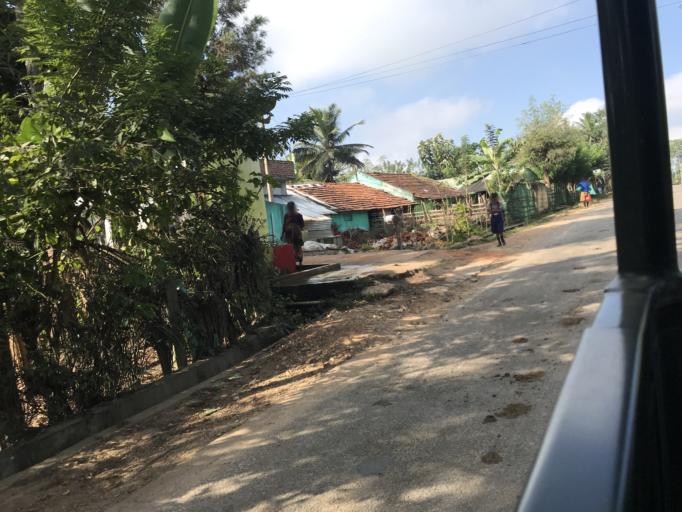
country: IN
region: Karnataka
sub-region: Mysore
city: Heggadadevankote
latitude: 11.9453
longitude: 76.2408
